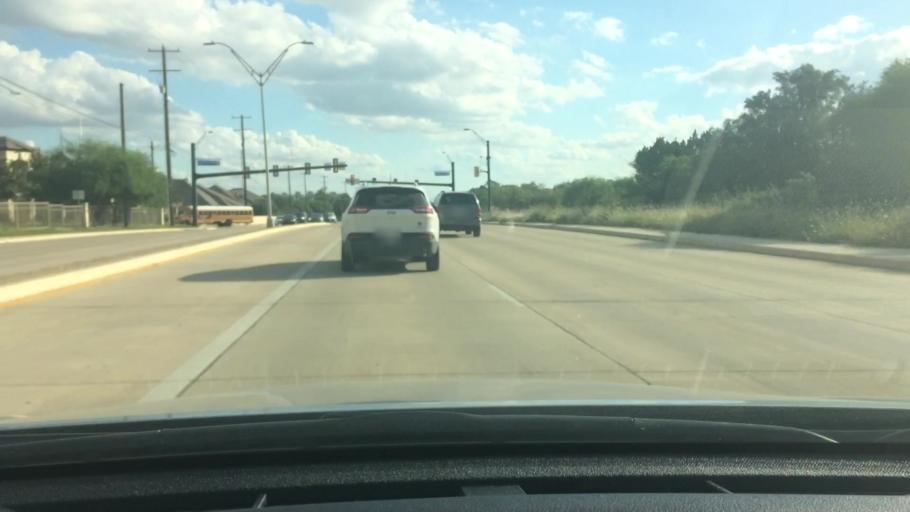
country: US
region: Texas
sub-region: Bexar County
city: Hollywood Park
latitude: 29.6320
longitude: -98.4235
